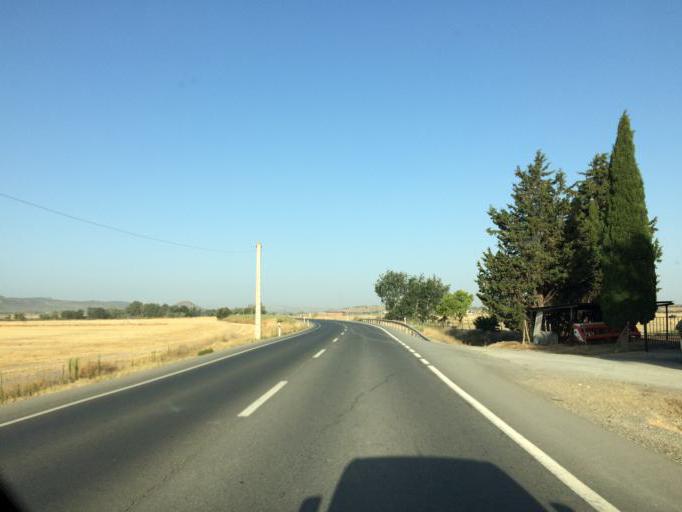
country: ES
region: Andalusia
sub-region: Provincia de Malaga
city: Mollina
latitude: 37.0564
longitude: -4.6340
